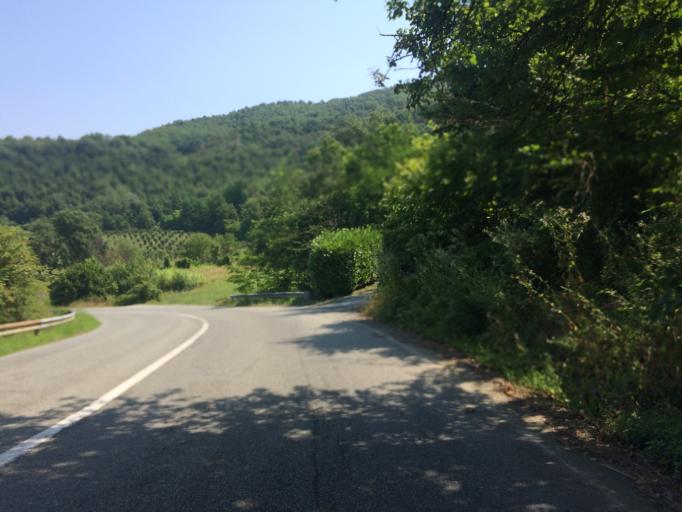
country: IT
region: Piedmont
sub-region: Provincia di Alessandria
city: Castelletto d'Erro
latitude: 44.6191
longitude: 8.4154
